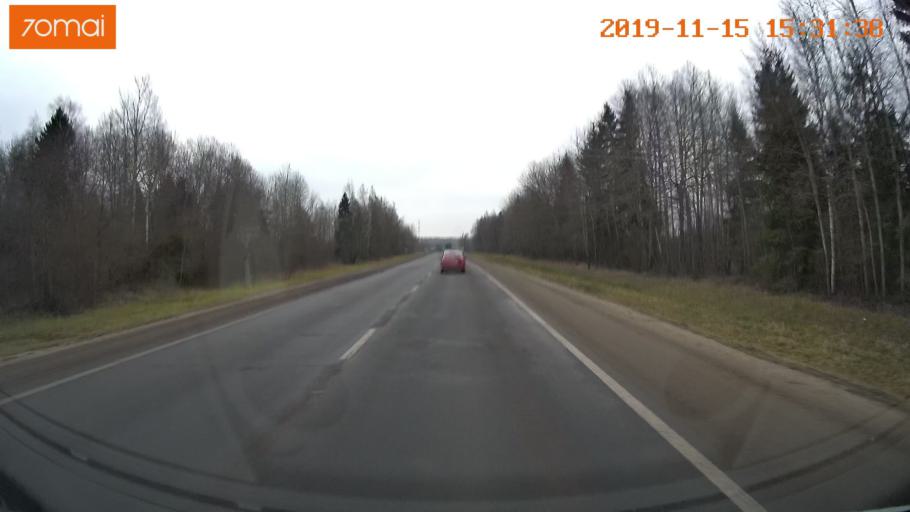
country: RU
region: Jaroslavl
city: Danilov
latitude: 58.0981
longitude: 40.1059
